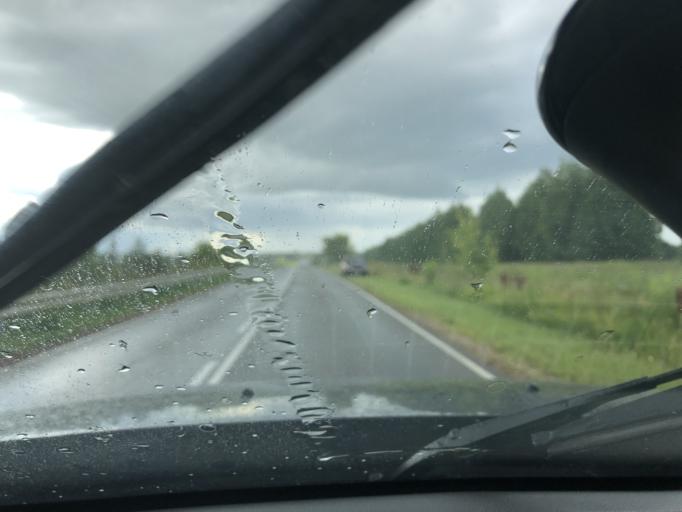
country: RU
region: Tula
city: Shvartsevskiy
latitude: 54.0782
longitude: 37.9199
